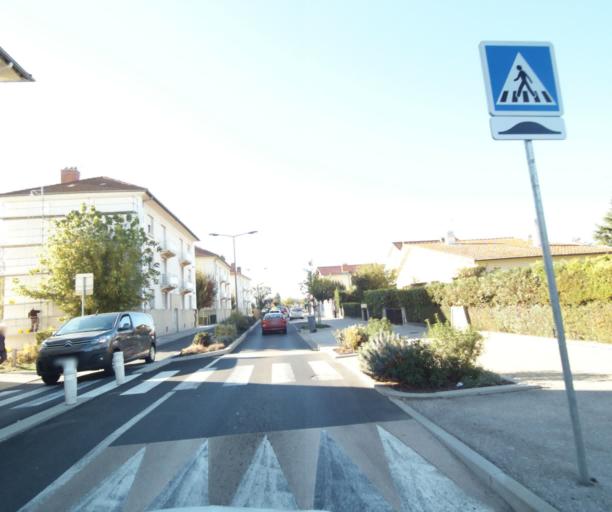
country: FR
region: Auvergne
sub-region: Departement du Puy-de-Dome
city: Gerzat
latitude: 45.8192
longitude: 3.1412
